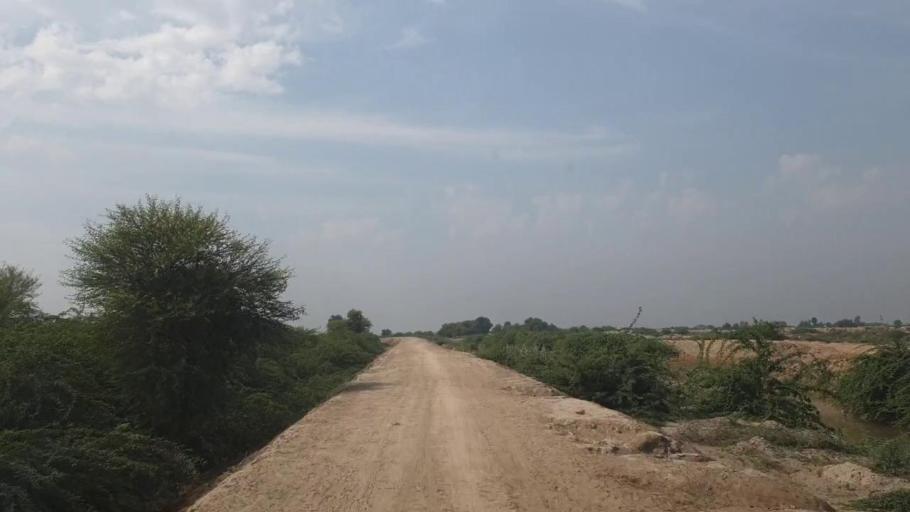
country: PK
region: Sindh
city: Rajo Khanani
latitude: 24.9680
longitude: 69.0082
